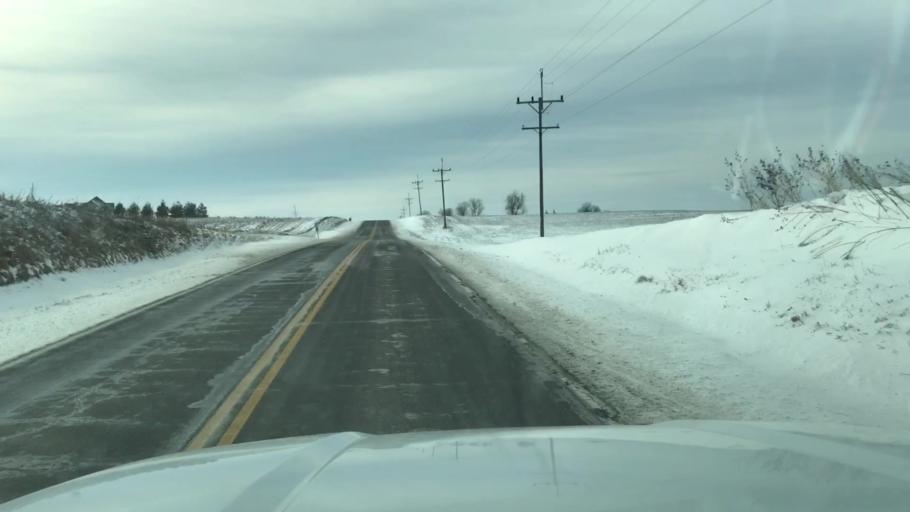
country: US
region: Missouri
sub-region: Holt County
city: Mound City
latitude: 40.1058
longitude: -95.1449
